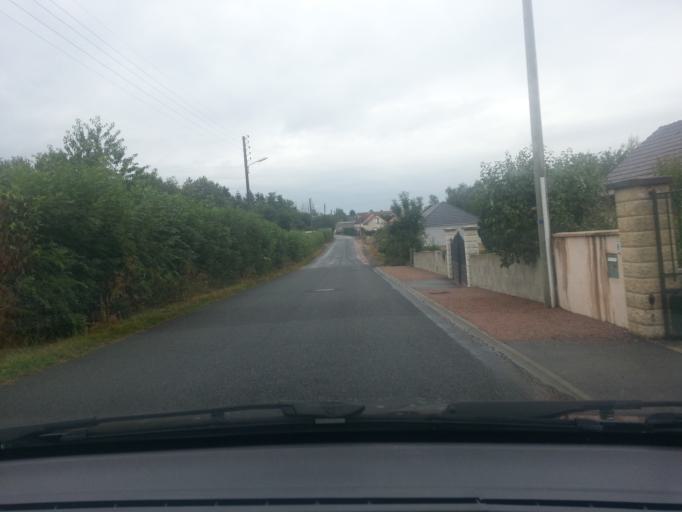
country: FR
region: Bourgogne
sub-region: Departement de Saone-et-Loire
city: Montchanin
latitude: 46.7424
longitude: 4.4600
